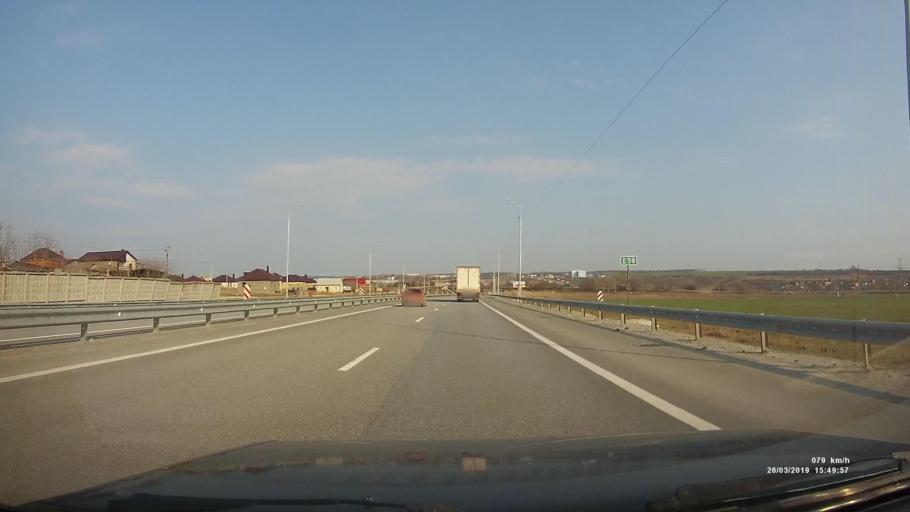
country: RU
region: Rostov
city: Chaltyr
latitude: 47.2749
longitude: 39.4780
